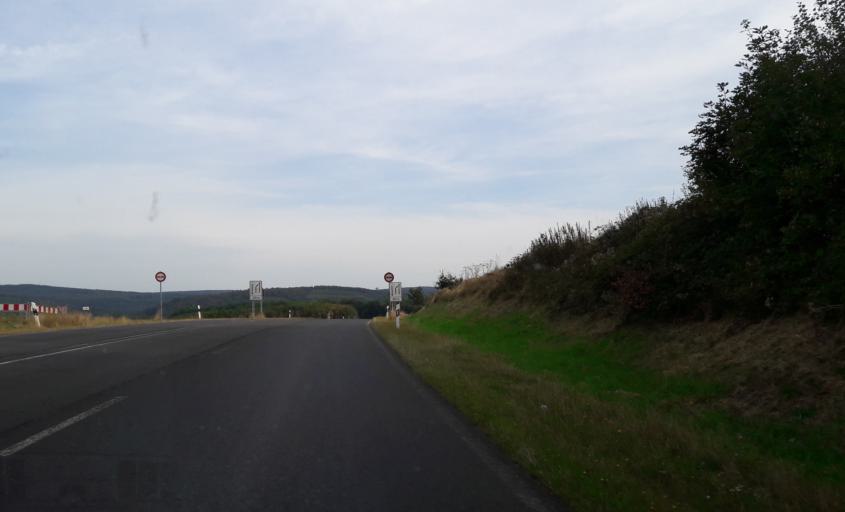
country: DE
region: Rheinland-Pfalz
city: Ellenberg
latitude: 49.6683
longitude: 7.1454
